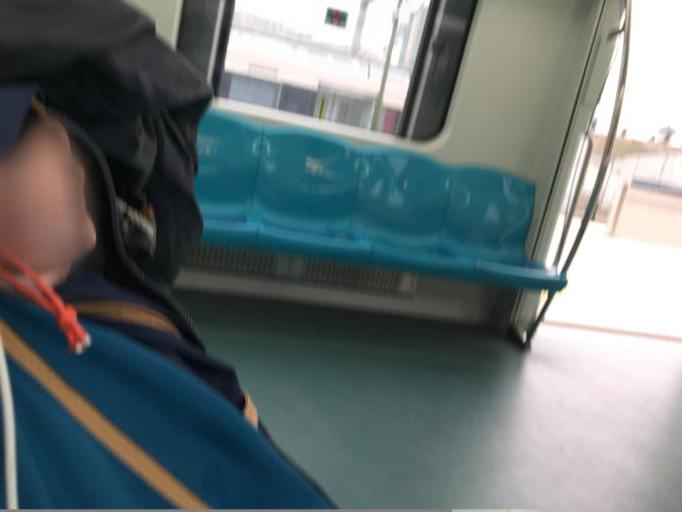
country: TR
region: Istanbul
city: Mahmutbey
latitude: 41.0175
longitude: 28.7667
